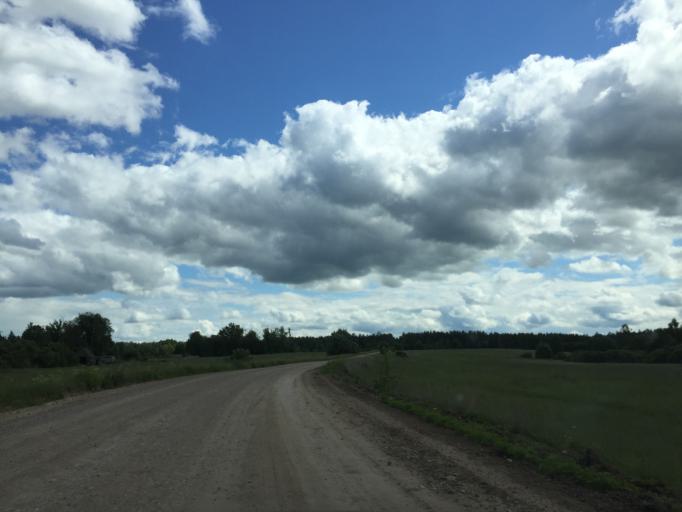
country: LV
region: Vecumnieki
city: Vecumnieki
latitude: 56.5024
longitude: 24.4059
